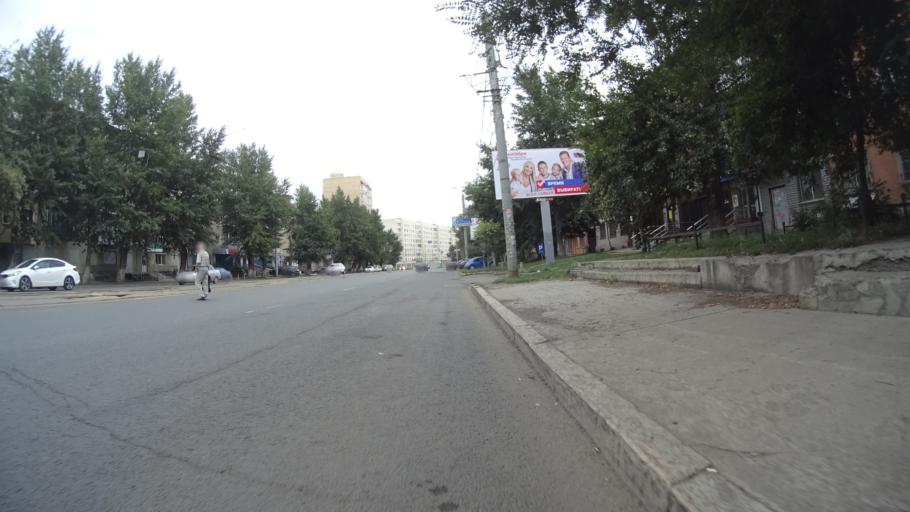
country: RU
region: Chelyabinsk
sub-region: Gorod Chelyabinsk
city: Chelyabinsk
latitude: 55.1515
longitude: 61.4102
